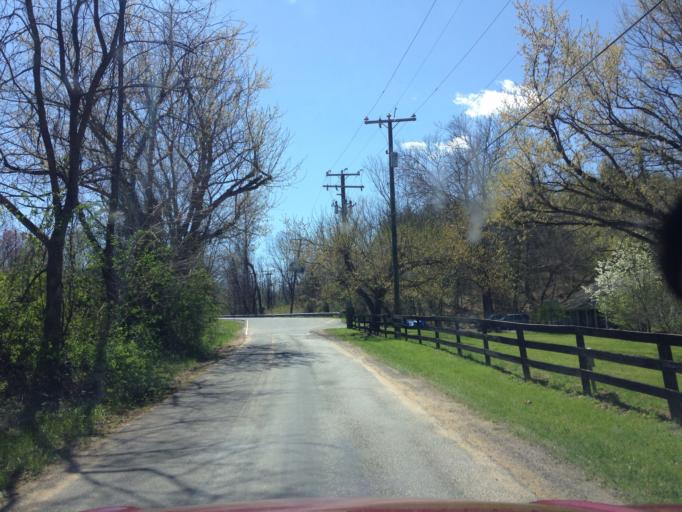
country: US
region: Maryland
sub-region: Frederick County
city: Brunswick
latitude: 39.2972
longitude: -77.6340
